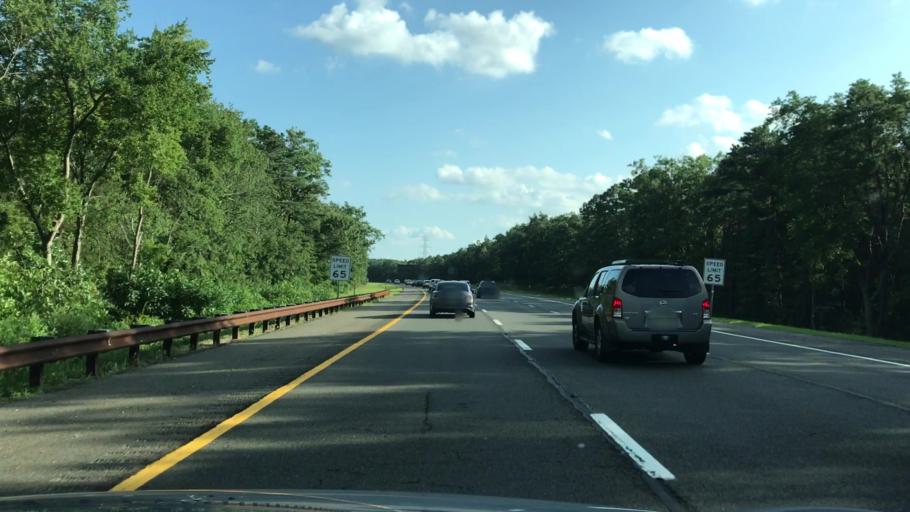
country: US
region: New Jersey
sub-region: Ocean County
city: Forked River
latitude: 39.8572
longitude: -74.2230
